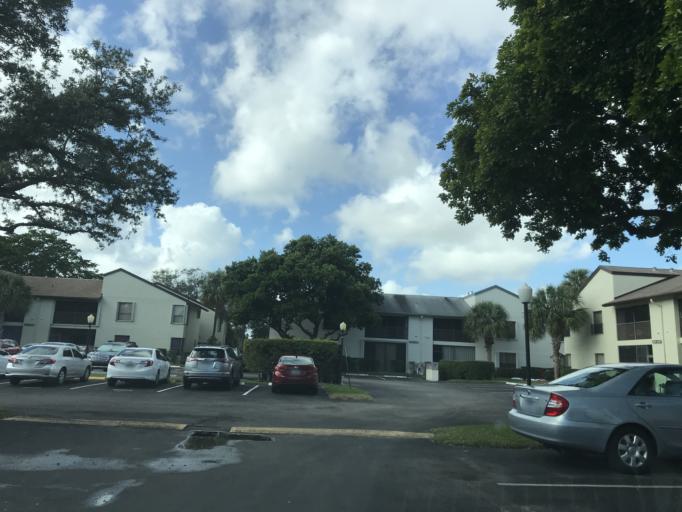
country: US
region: Florida
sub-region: Broward County
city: Coconut Creek
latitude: 26.2669
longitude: -80.1915
